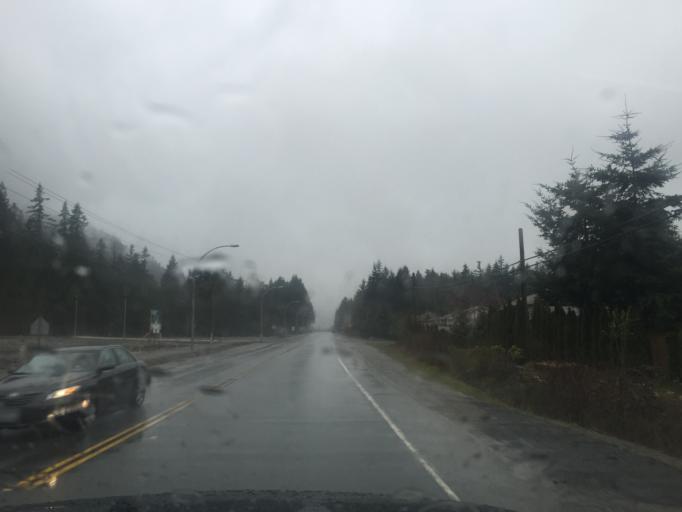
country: CA
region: British Columbia
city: Hope
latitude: 49.3612
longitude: -121.4672
